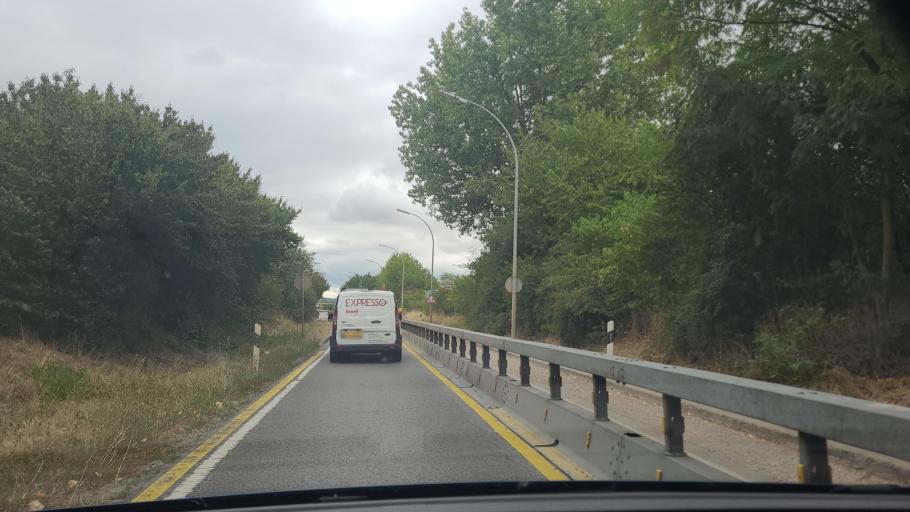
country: LU
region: Luxembourg
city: Lamadelaine
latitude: 49.5565
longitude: 5.8618
